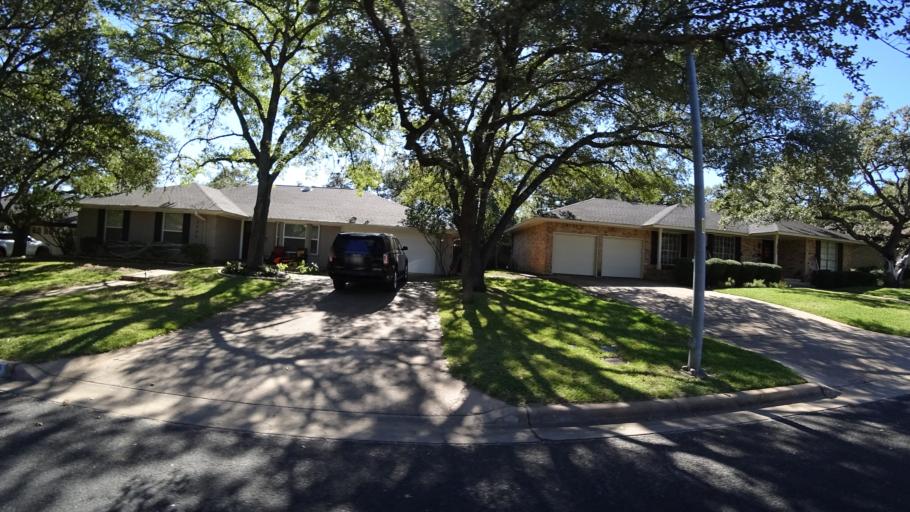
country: US
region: Texas
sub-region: Travis County
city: West Lake Hills
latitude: 30.3624
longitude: -97.7581
